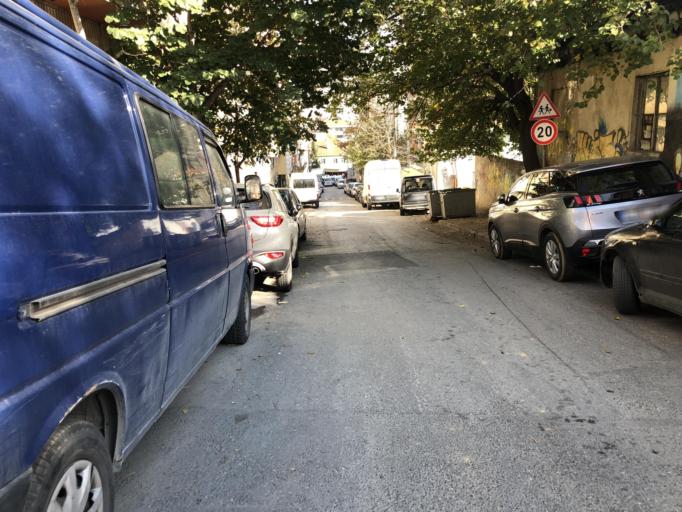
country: TR
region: Istanbul
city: Esenler
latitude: 41.0708
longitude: 28.9015
